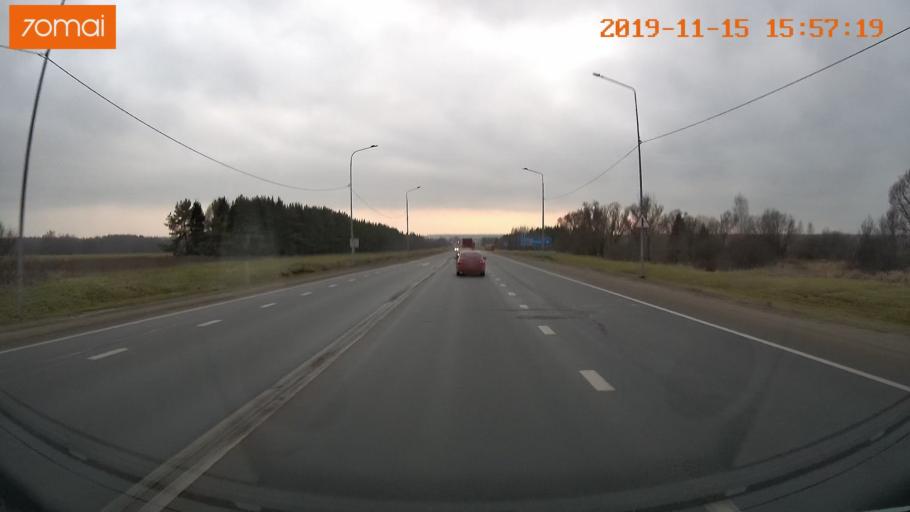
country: RU
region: Jaroslavl
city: Yaroslavl
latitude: 57.8316
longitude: 39.9646
